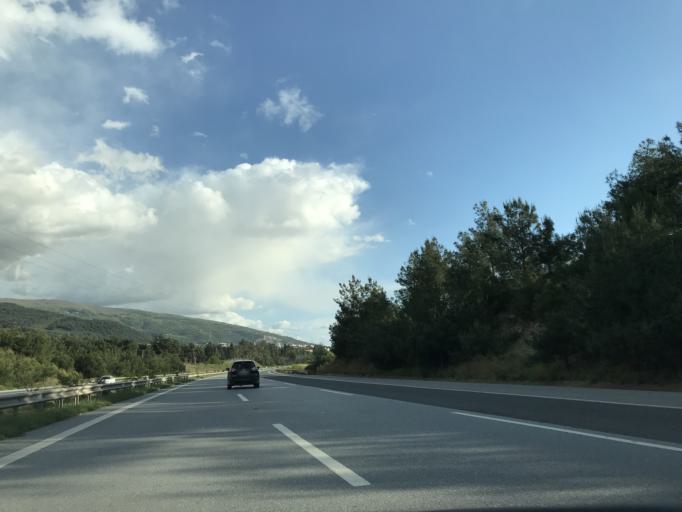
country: TR
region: Hatay
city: Yakacik
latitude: 36.7259
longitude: 36.2240
